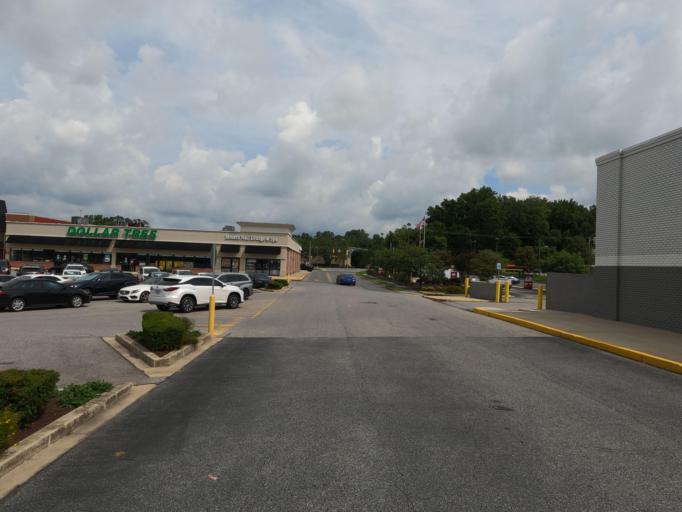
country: US
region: Maryland
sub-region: Anne Arundel County
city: Crofton
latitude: 39.0169
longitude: -76.6940
